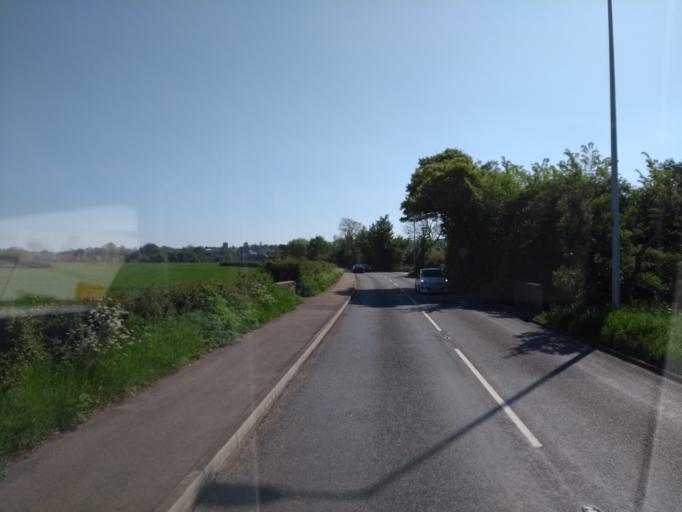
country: GB
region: England
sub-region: Devon
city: Axminster
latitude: 50.7783
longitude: -3.0135
